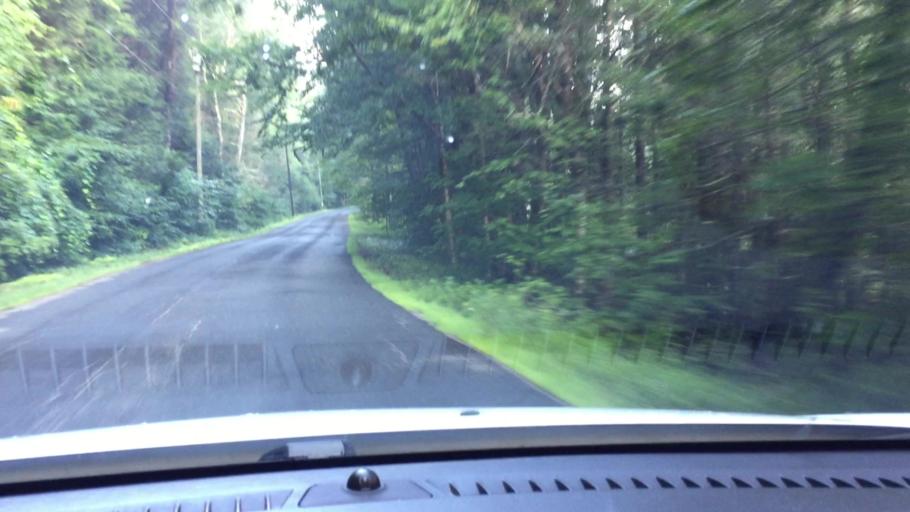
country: US
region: Massachusetts
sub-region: Berkshire County
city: Becket
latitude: 42.3727
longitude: -72.9687
